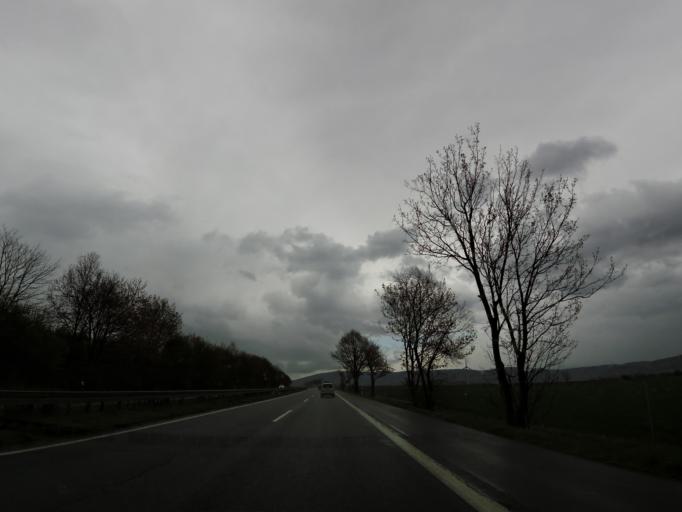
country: DE
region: Lower Saxony
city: Bad Harzburg
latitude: 51.9128
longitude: 10.5316
